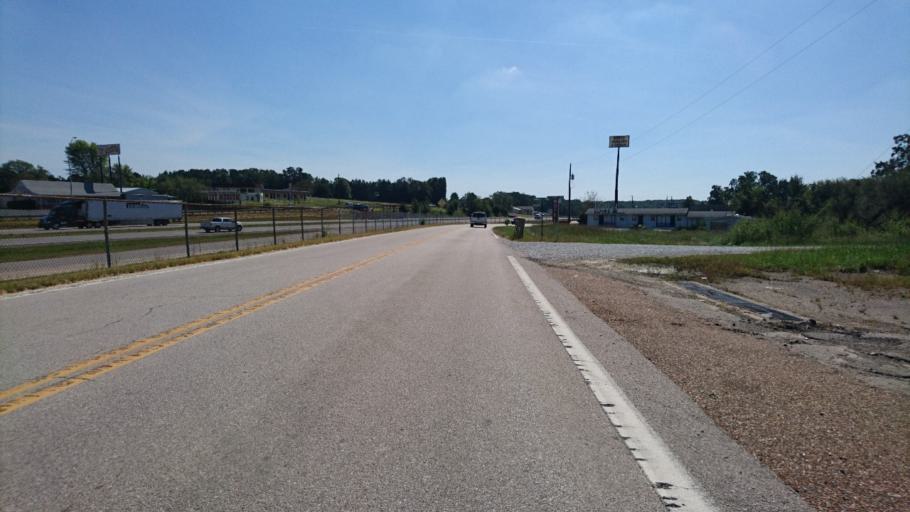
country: US
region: Missouri
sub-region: Franklin County
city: Sullivan
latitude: 38.2736
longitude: -91.1086
